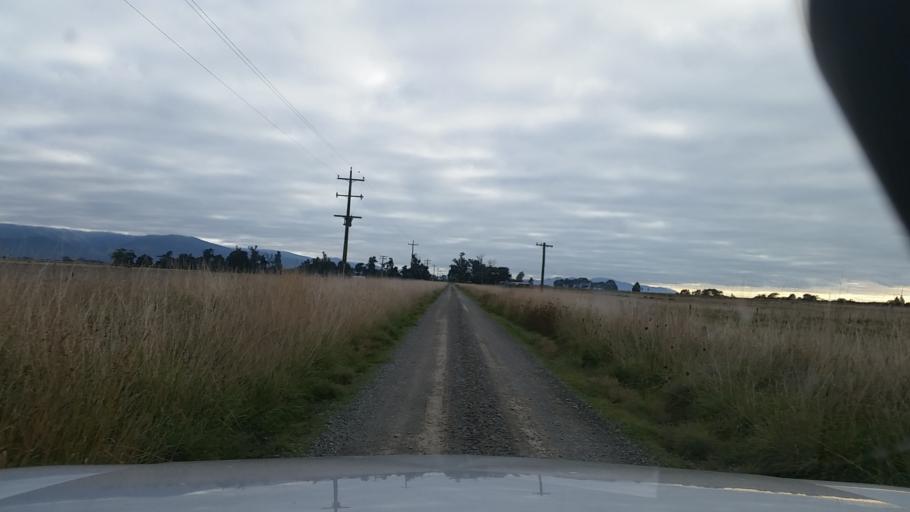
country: NZ
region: Marlborough
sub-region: Marlborough District
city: Blenheim
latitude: -41.5057
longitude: 174.0310
